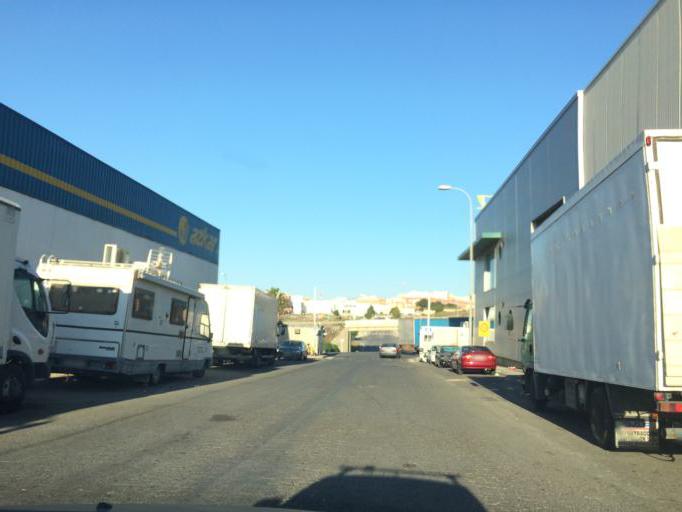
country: ES
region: Andalusia
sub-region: Provincia de Almeria
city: Viator
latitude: 36.8838
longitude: -2.4194
